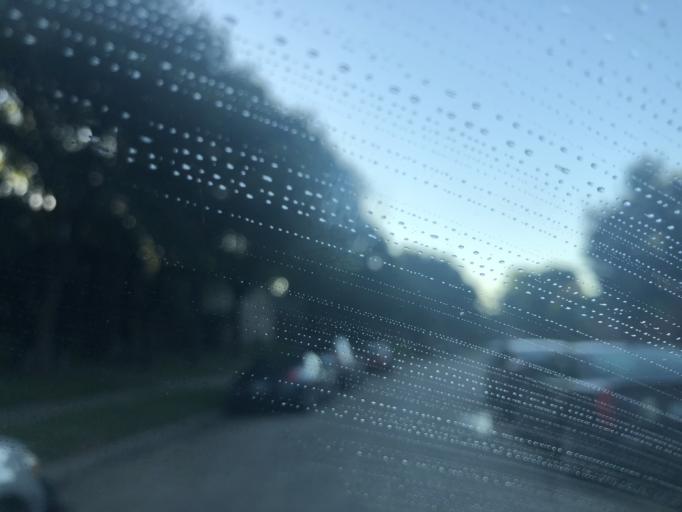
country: US
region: Texas
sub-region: Dallas County
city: Grand Prairie
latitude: 32.6690
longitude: -96.9954
